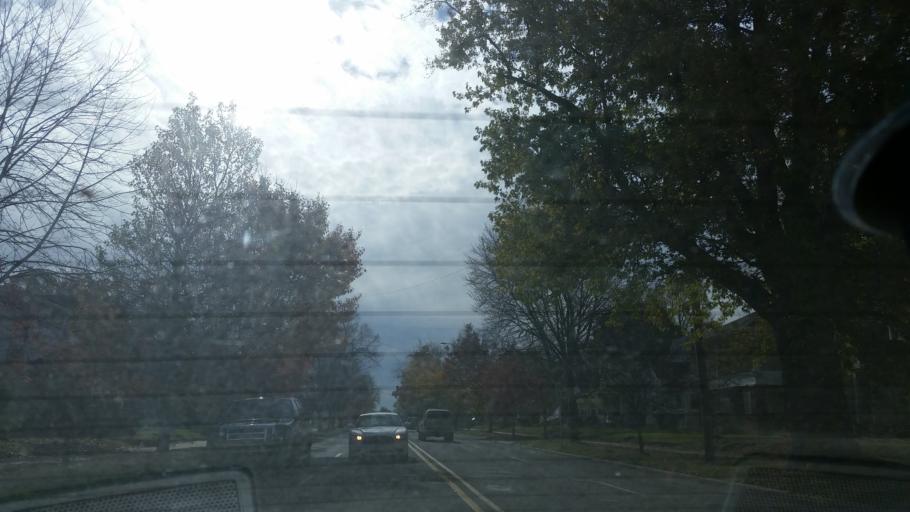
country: US
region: Indiana
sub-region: Howard County
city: Kokomo
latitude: 40.4800
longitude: -86.1336
